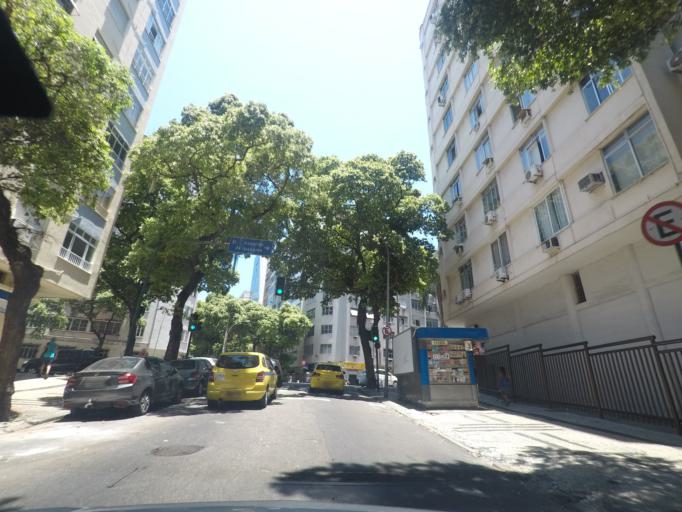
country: BR
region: Rio de Janeiro
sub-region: Rio De Janeiro
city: Rio de Janeiro
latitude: -22.9833
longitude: -43.1942
